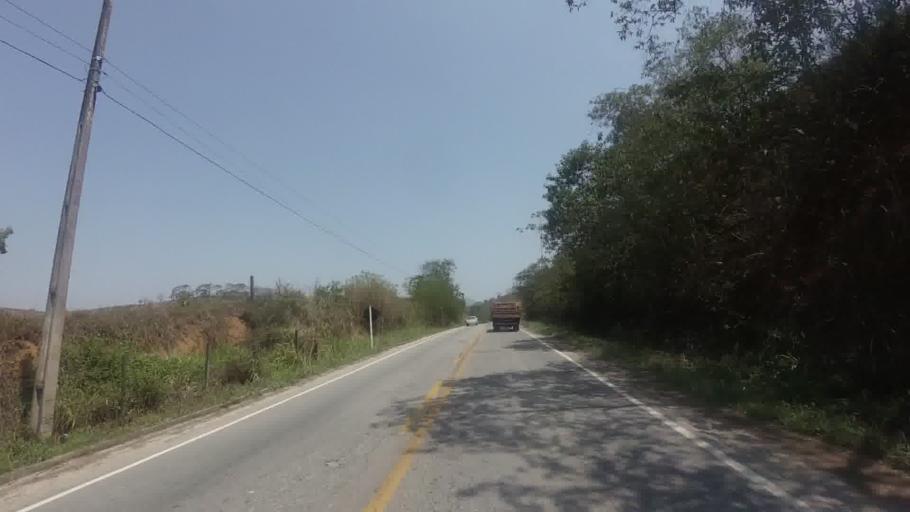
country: BR
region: Espirito Santo
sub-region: Cachoeiro De Itapemirim
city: Cachoeiro de Itapemirim
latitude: -20.8693
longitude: -41.0296
